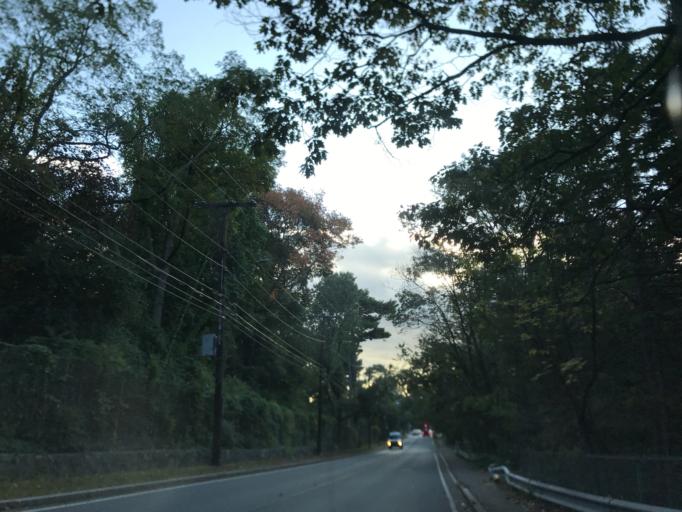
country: US
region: Massachusetts
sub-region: Suffolk County
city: Jamaica Plain
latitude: 42.3013
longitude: -71.1314
